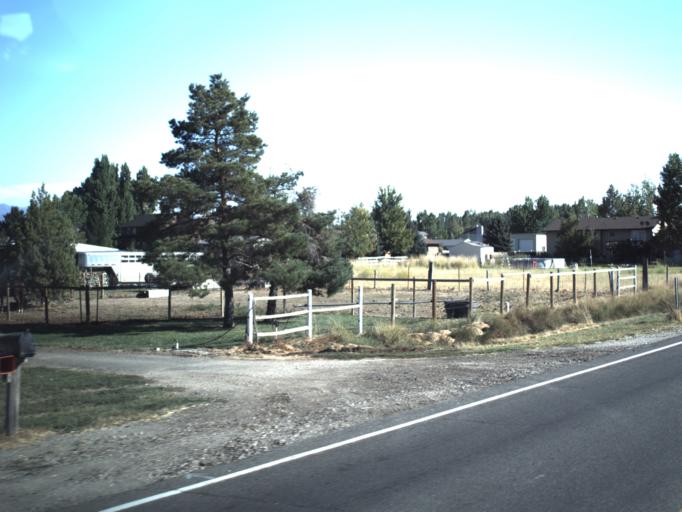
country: US
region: Utah
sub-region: Weber County
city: Hooper
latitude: 41.1877
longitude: -112.1226
